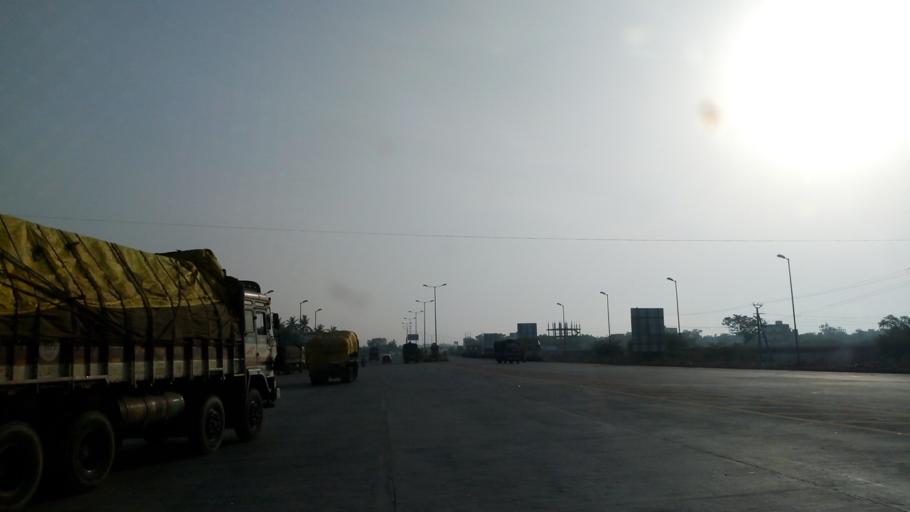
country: IN
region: Andhra Pradesh
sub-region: Guntur
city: Mangalagiri
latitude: 16.3864
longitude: 80.5342
